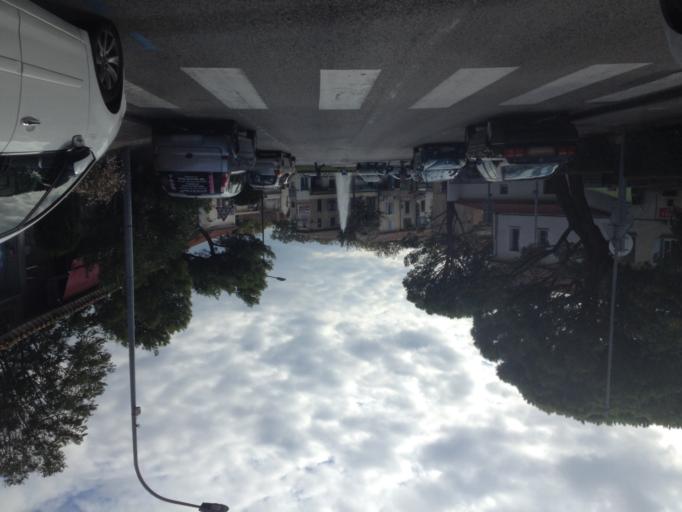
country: FR
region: Provence-Alpes-Cote d'Azur
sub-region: Departement du Vaucluse
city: Sorgues
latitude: 44.0087
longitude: 4.8738
